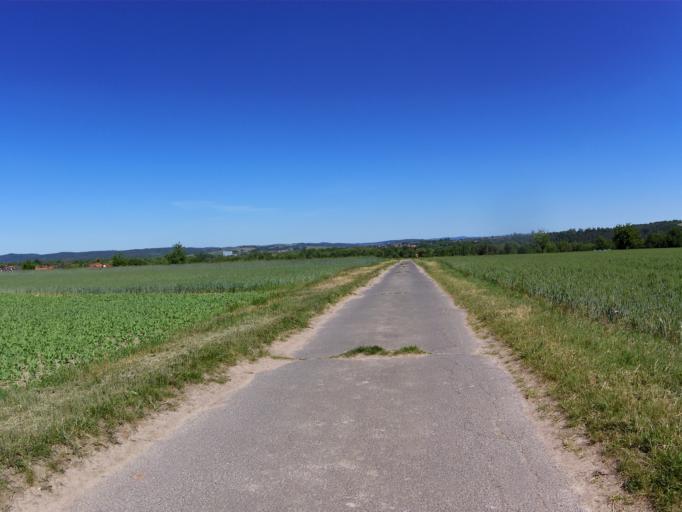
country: DE
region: Thuringia
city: Dankmarshausen
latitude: 50.9406
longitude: 10.0346
